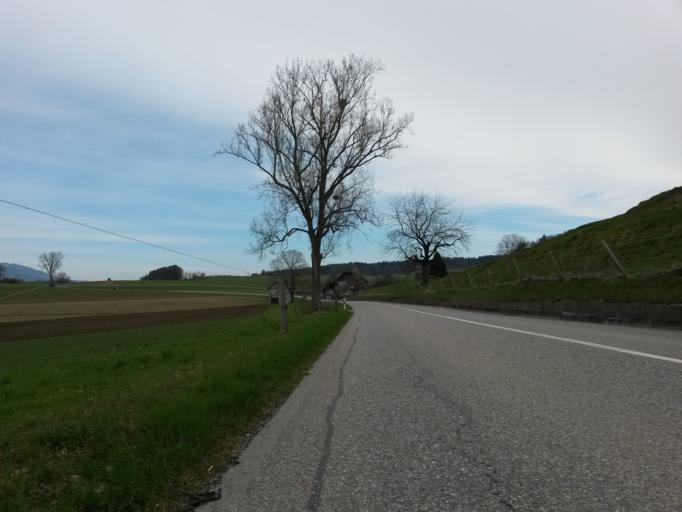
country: CH
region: Bern
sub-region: Seeland District
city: Leuzigen
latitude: 47.1802
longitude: 7.4756
